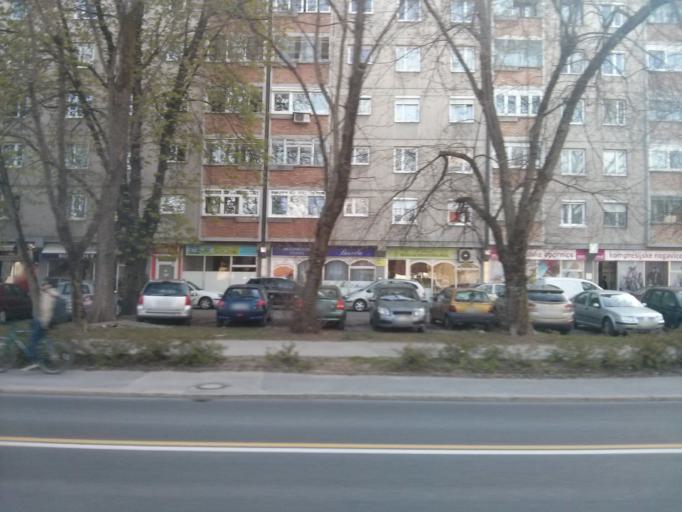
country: SI
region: Ljubljana
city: Ljubljana
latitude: 46.0654
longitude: 14.4933
